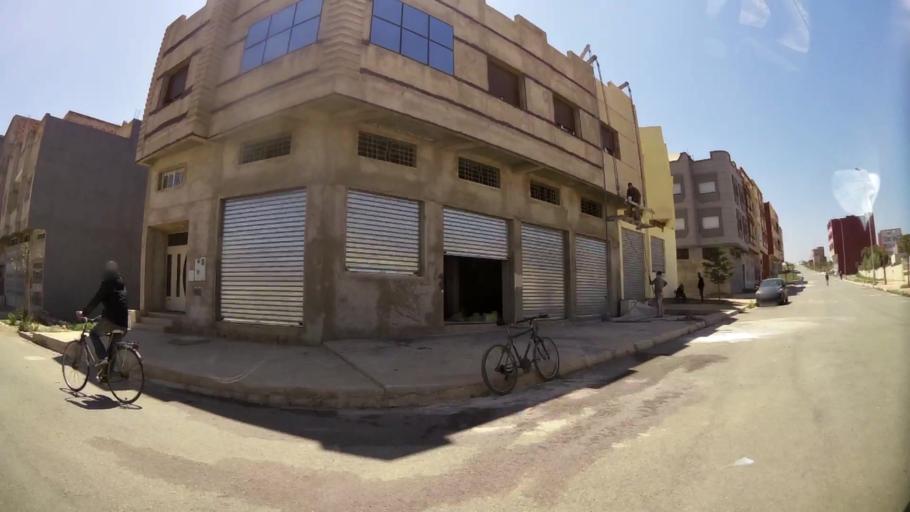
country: MA
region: Oriental
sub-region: Oujda-Angad
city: Oujda
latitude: 34.6824
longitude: -1.9488
